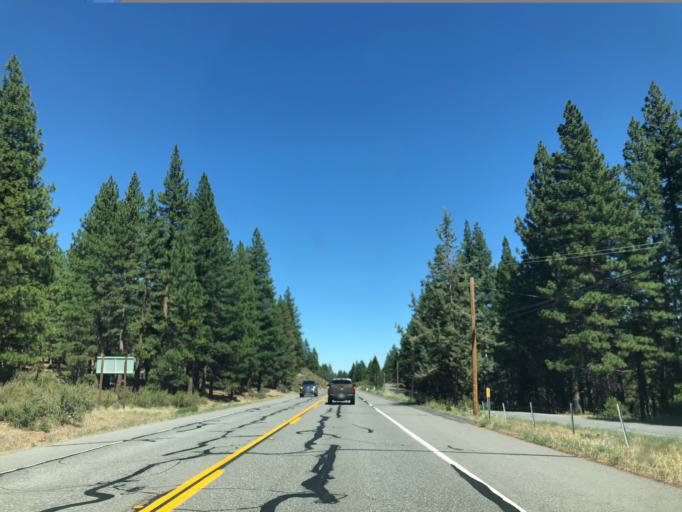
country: US
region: California
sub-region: Lassen County
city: Susanville
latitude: 40.4150
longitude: -120.7352
